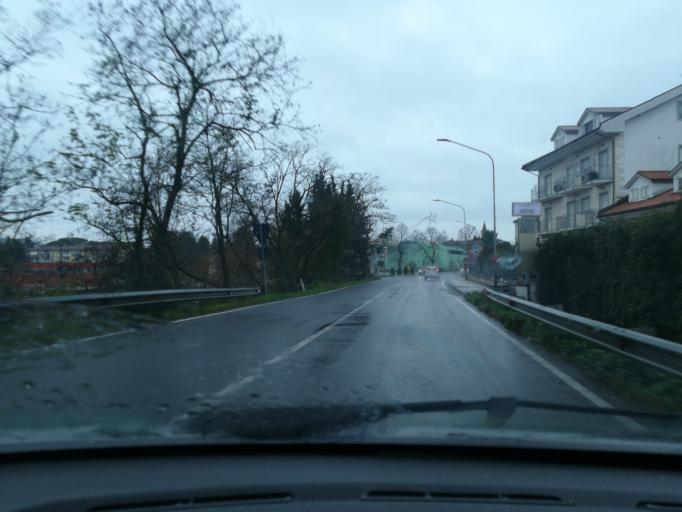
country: IT
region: The Marches
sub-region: Provincia di Macerata
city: Sforzacosta
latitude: 43.2590
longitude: 13.4220
